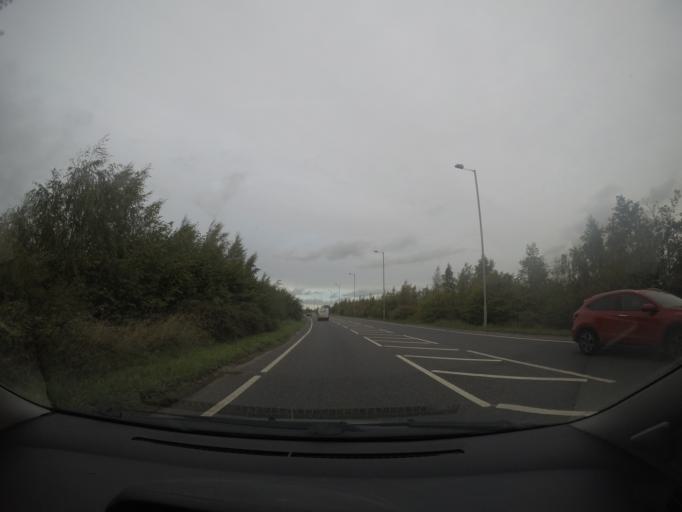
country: GB
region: England
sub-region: North Yorkshire
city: Barlby
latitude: 53.7831
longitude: -1.0363
